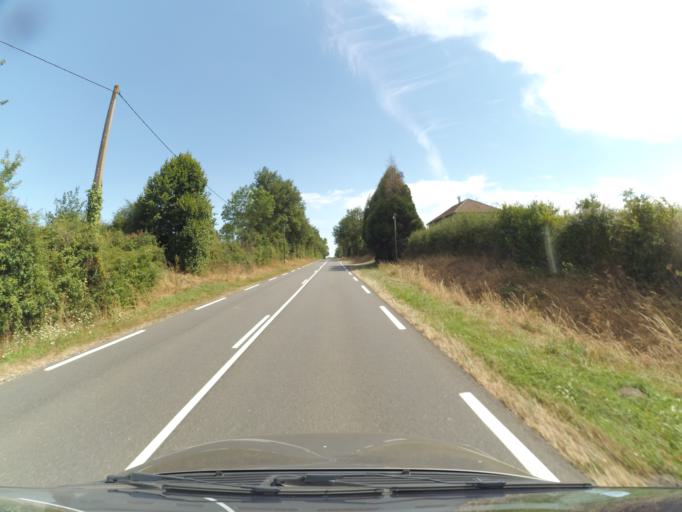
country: FR
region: Poitou-Charentes
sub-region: Departement de la Charente
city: Etagnac
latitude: 45.9387
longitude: 0.7320
